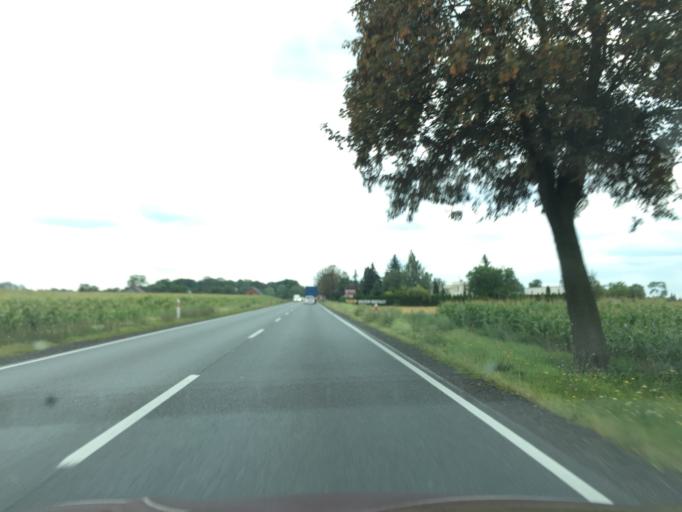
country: PL
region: Greater Poland Voivodeship
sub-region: Kalisz
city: Kalisz
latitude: 51.8196
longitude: 18.0934
